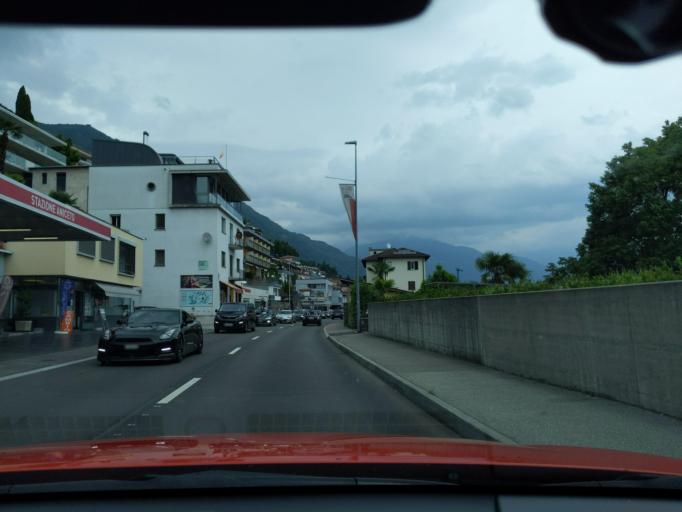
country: CH
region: Ticino
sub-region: Locarno District
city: Brissago
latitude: 46.1158
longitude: 8.7075
